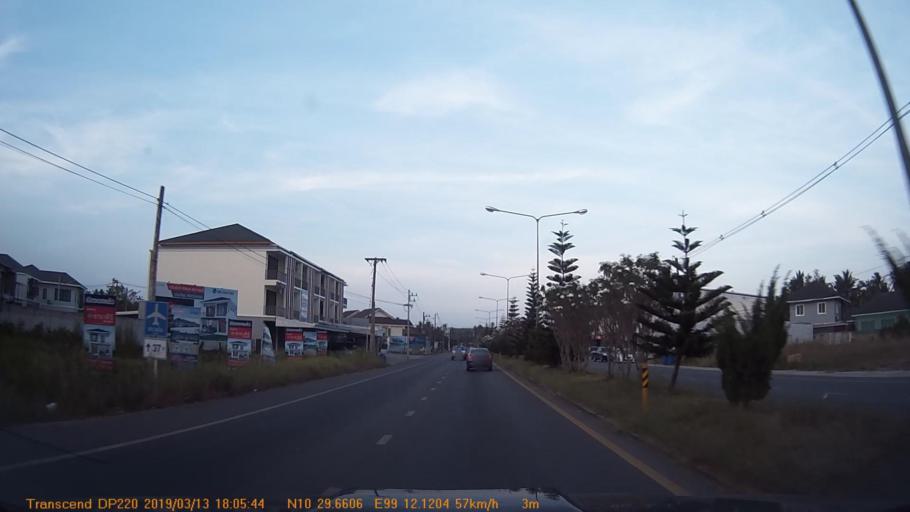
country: TH
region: Chumphon
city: Chumphon
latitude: 10.4947
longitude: 99.2023
